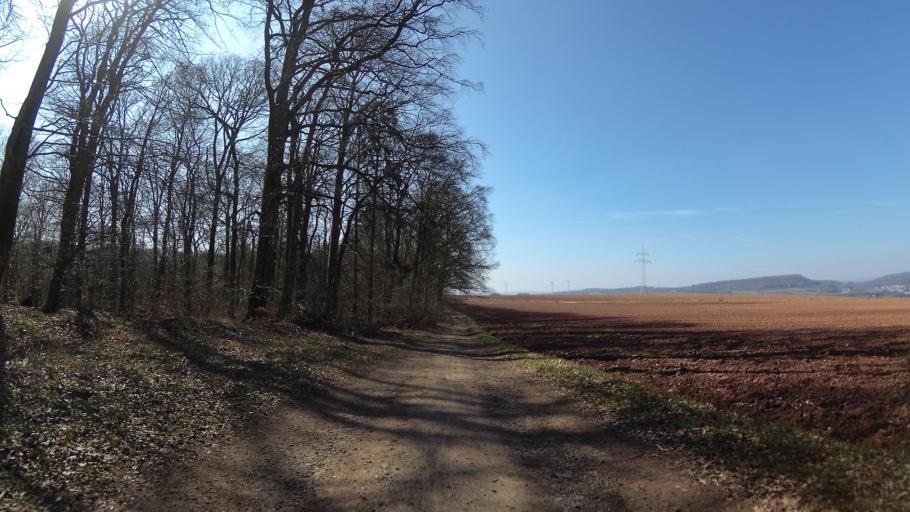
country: DE
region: Saarland
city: Eppelborn
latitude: 49.4341
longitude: 6.9817
